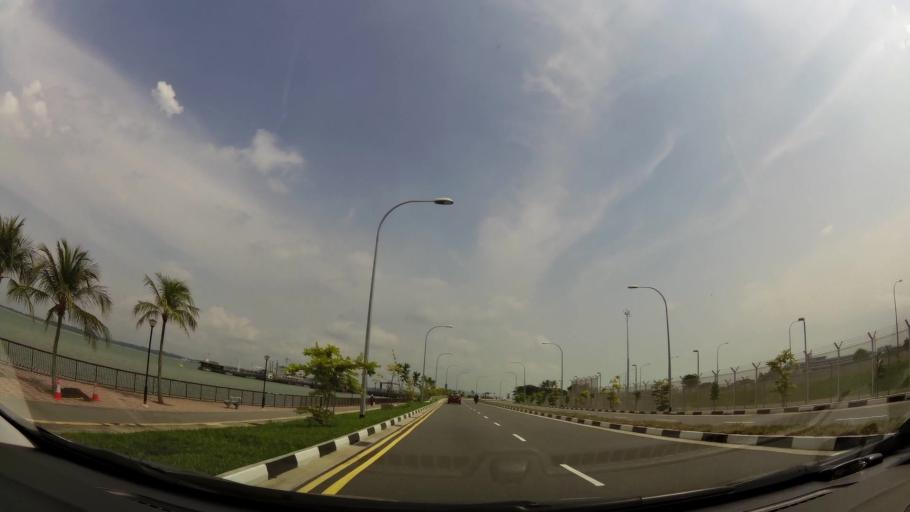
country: MY
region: Johor
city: Kampung Pasir Gudang Baru
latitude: 1.3897
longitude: 103.9963
